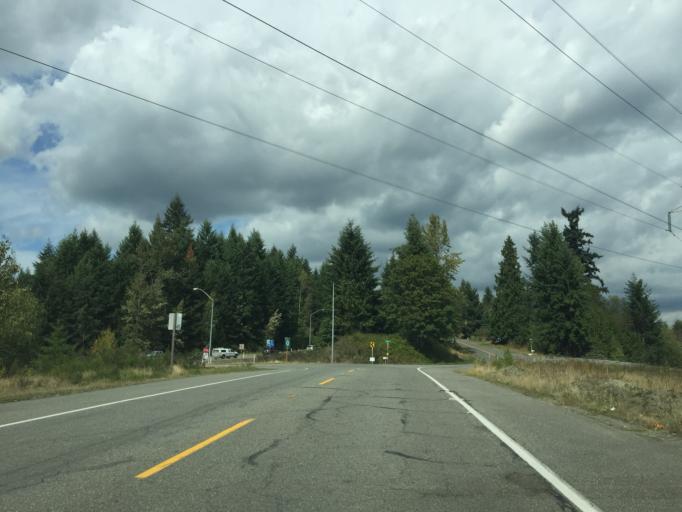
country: US
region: Washington
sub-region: Snohomish County
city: Snohomish
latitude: 47.9329
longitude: -122.1004
